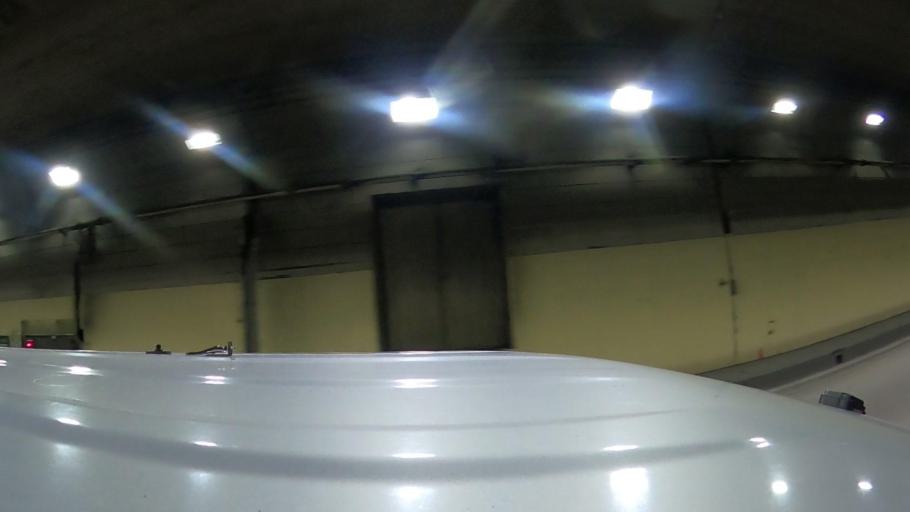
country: JP
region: Kanagawa
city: Yokohama
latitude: 35.4591
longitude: 139.6231
